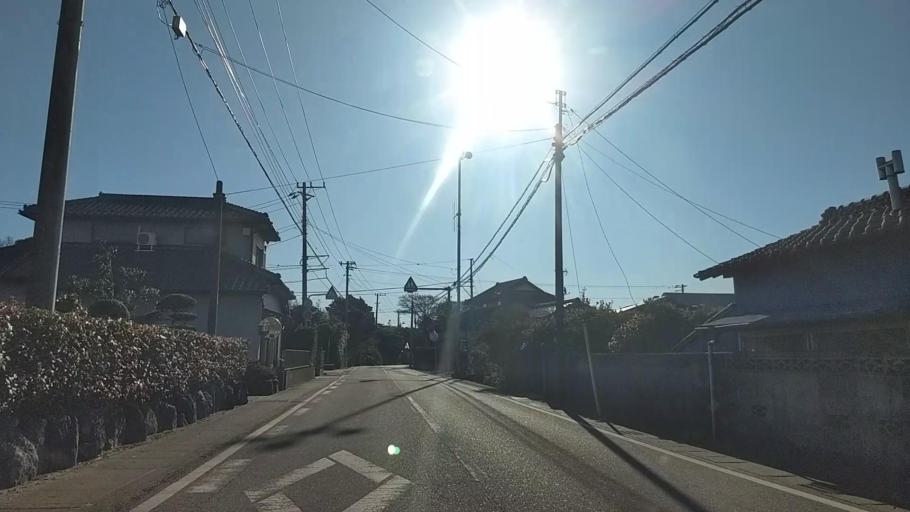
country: JP
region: Chiba
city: Futtsu
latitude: 35.3042
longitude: 139.8338
